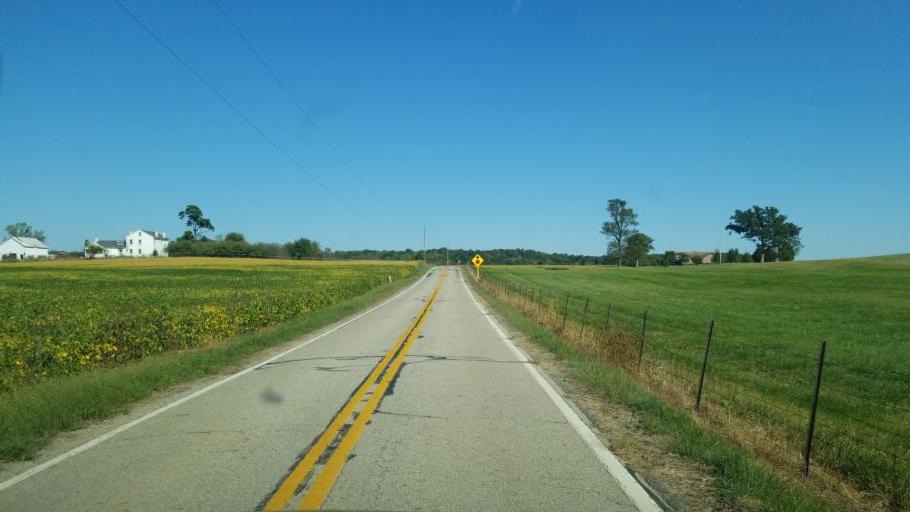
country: US
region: Ohio
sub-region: Clark County
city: Northridge
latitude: 39.9603
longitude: -83.6830
